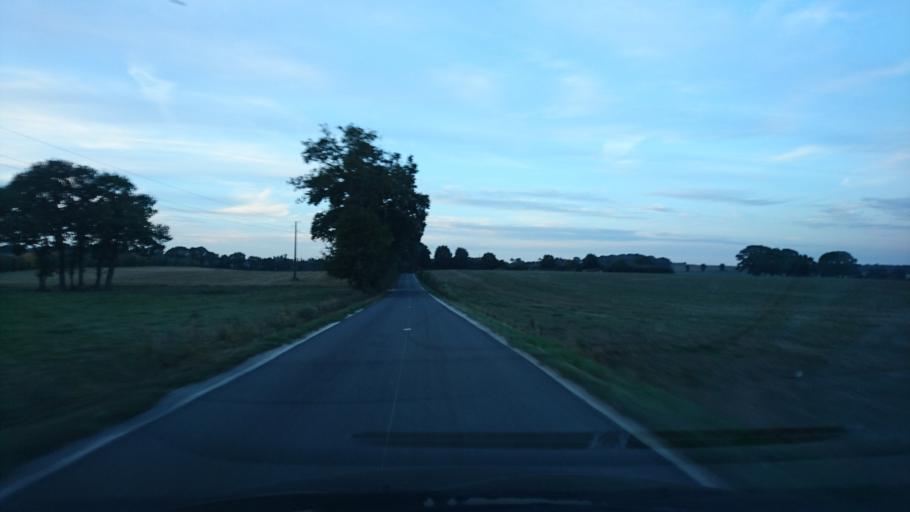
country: FR
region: Brittany
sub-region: Departement d'Ille-et-Vilaine
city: Guignen
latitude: 47.8716
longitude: -1.8882
